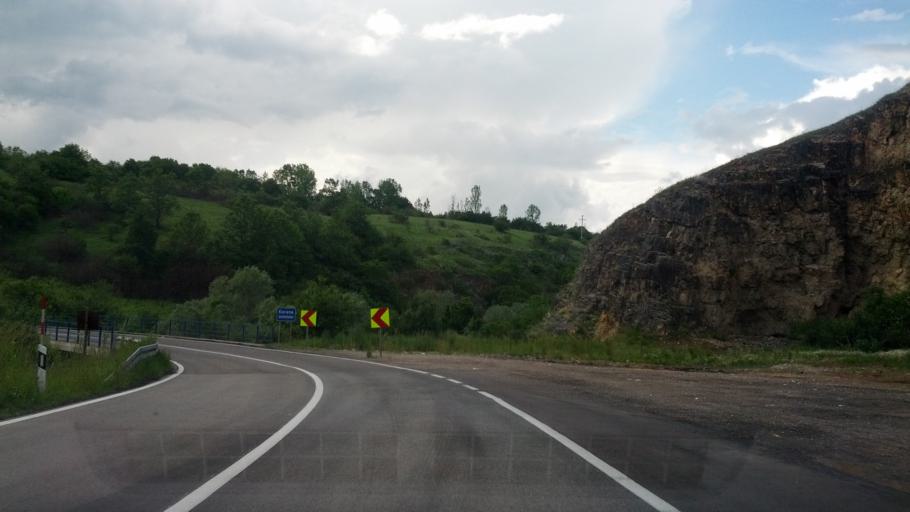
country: BA
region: Federation of Bosnia and Herzegovina
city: Izacic
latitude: 44.9195
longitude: 15.7124
